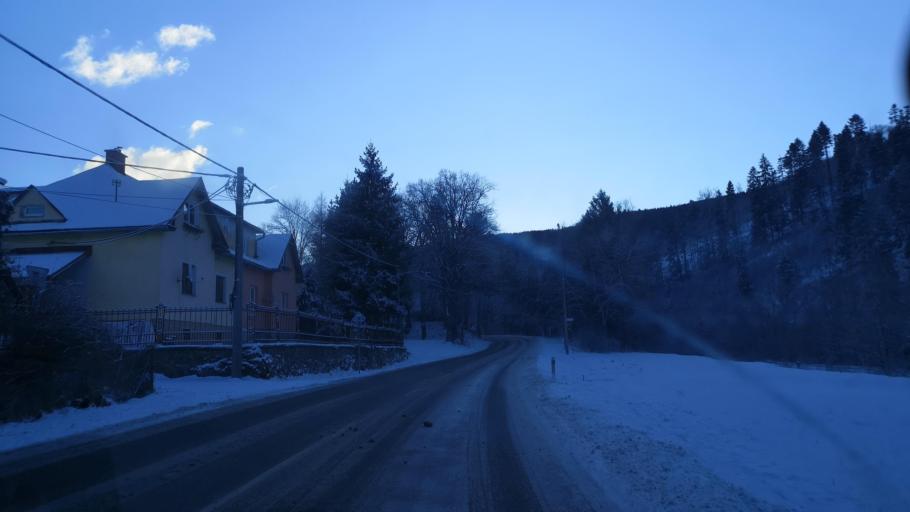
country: SK
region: Banskobystricky
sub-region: Okres Banska Bystrica
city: Brezno
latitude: 48.8285
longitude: 19.7625
